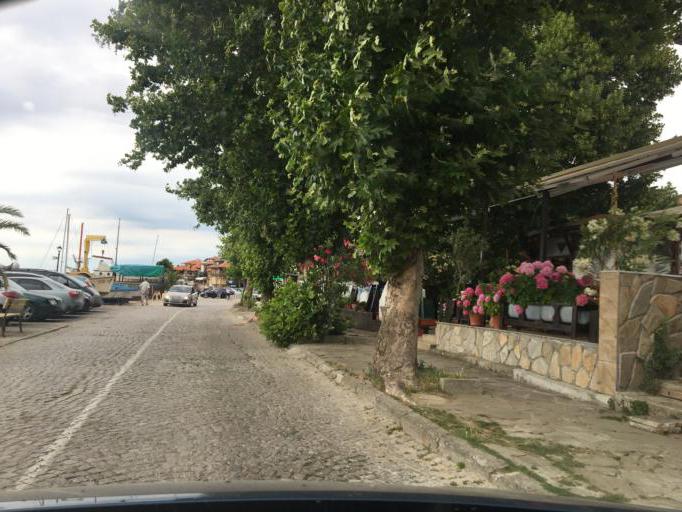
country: BG
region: Burgas
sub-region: Obshtina Sozopol
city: Sozopol
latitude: 42.4236
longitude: 27.6929
